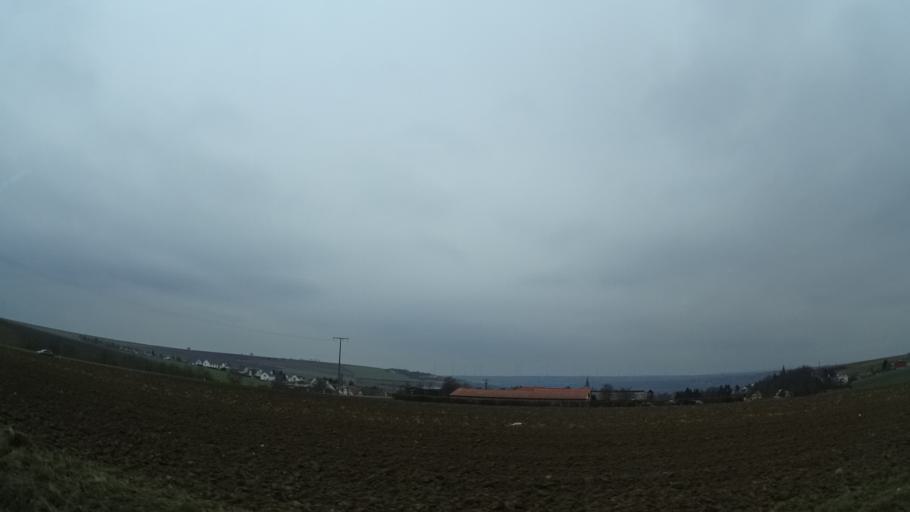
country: DE
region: Rheinland-Pfalz
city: Stetten
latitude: 49.6751
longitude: 8.0880
